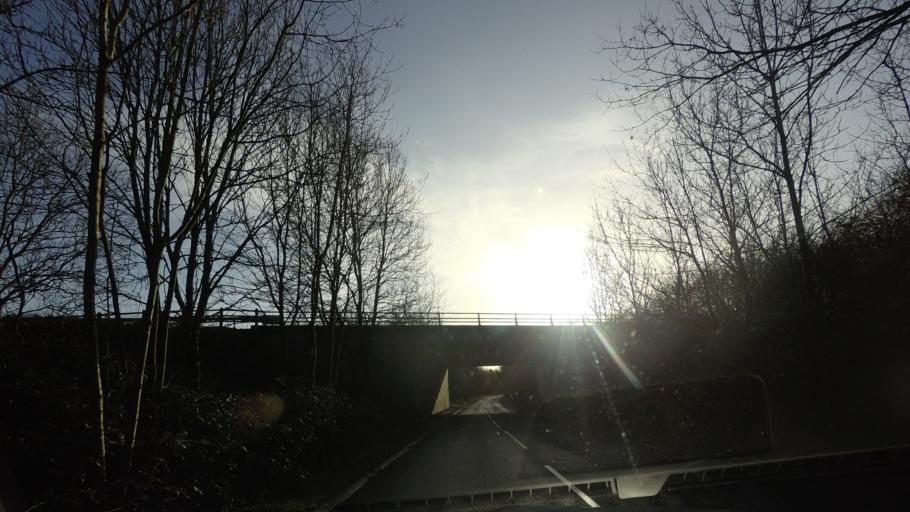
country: GB
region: England
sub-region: Kent
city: Borough Green
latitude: 51.3025
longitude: 0.2859
